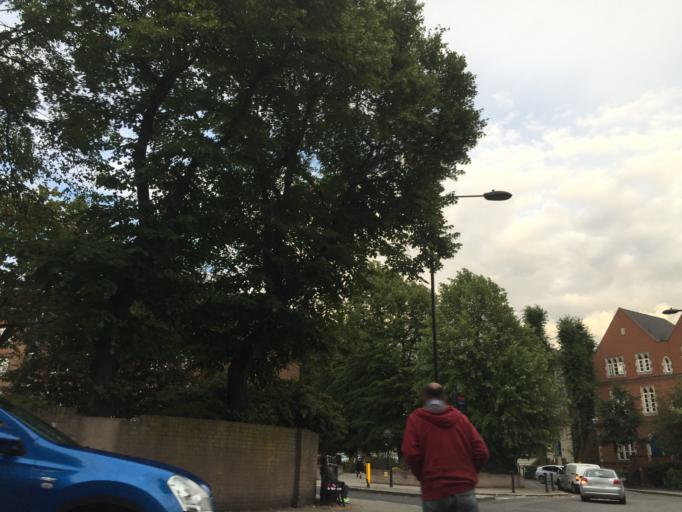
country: GB
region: England
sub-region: Greater London
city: Belsize Park
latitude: 51.5421
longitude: -0.1797
